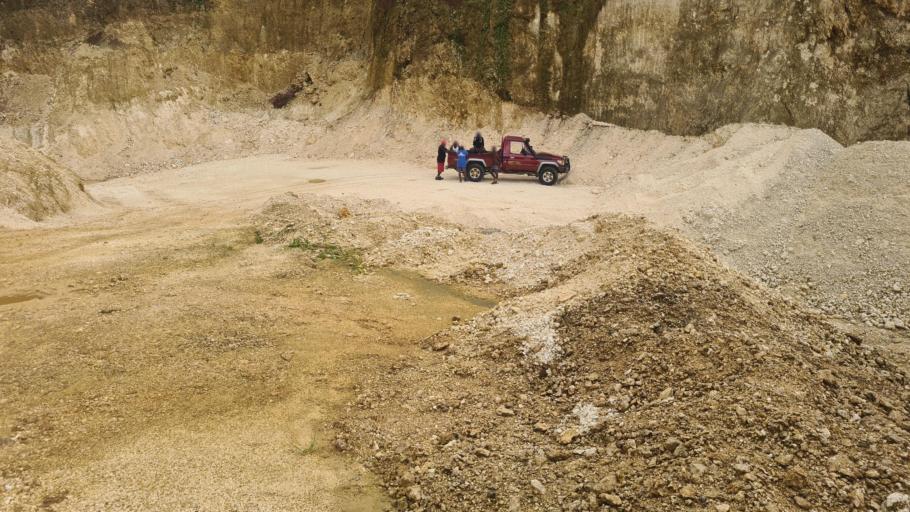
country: VU
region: Penama
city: Saratamata
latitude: -15.9666
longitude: 168.2157
